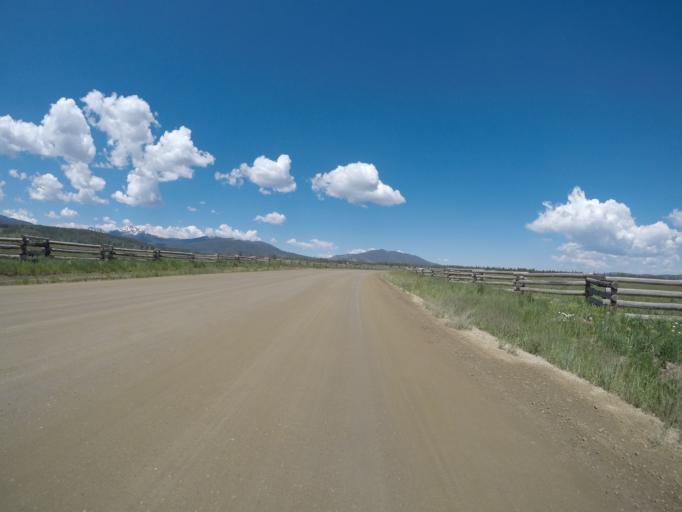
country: US
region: Colorado
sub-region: Grand County
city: Fraser
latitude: 39.9400
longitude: -105.8200
